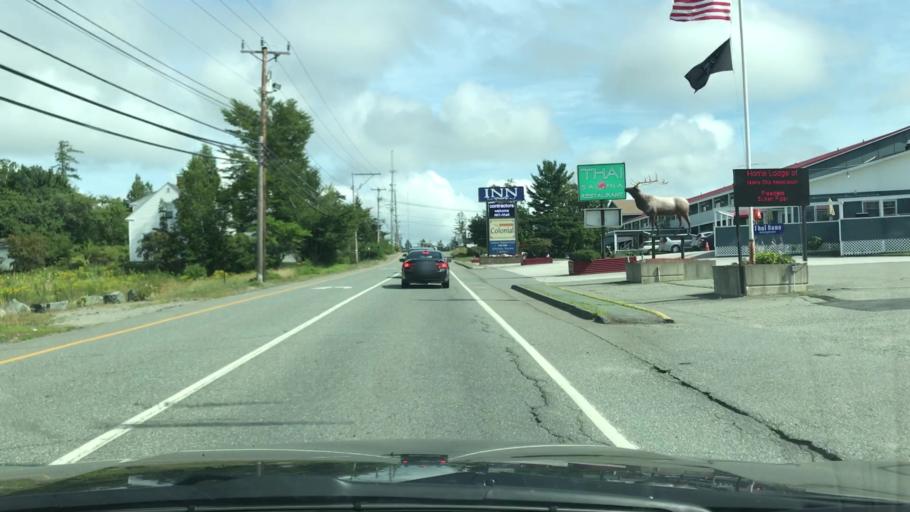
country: US
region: Maine
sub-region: Hancock County
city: Ellsworth
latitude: 44.5263
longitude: -68.4008
